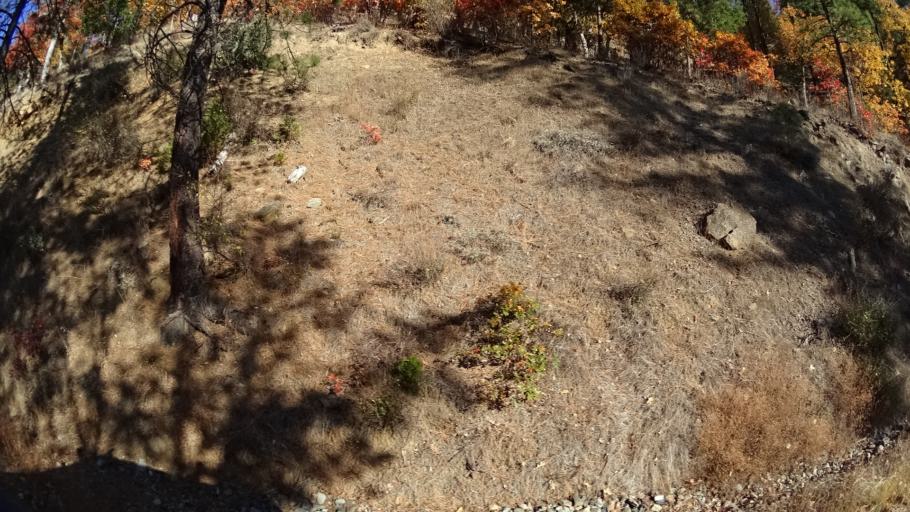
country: US
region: California
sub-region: Siskiyou County
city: Happy Camp
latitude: 41.6454
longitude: -123.0327
